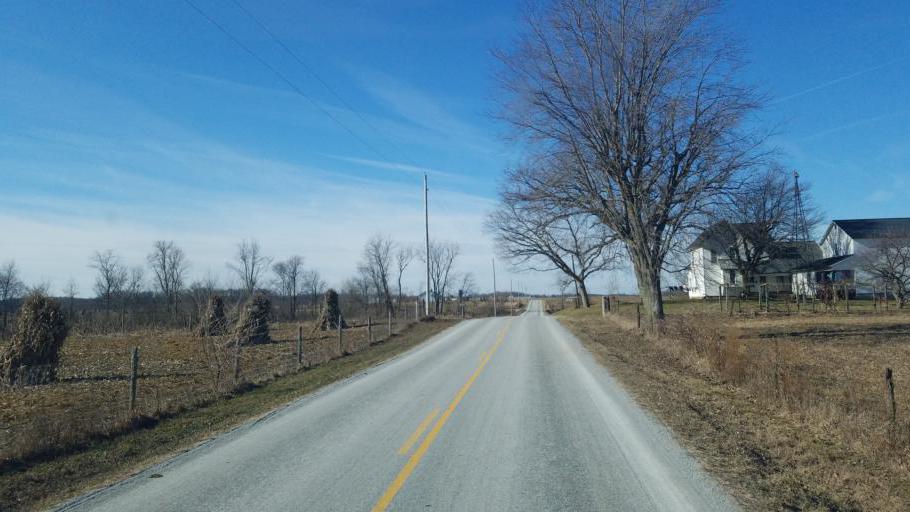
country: US
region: Ohio
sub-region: Hardin County
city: Kenton
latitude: 40.5739
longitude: -83.4464
